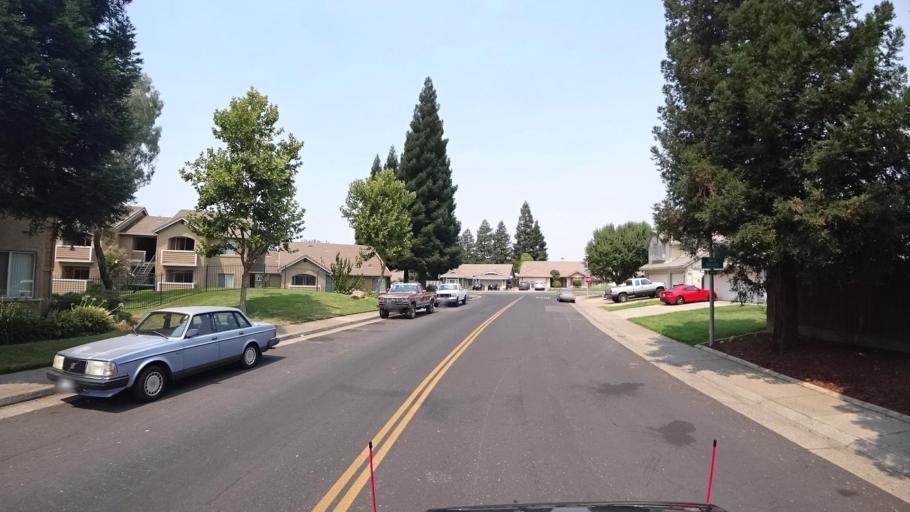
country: US
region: California
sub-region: Placer County
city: Rocklin
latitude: 38.8005
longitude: -121.2637
